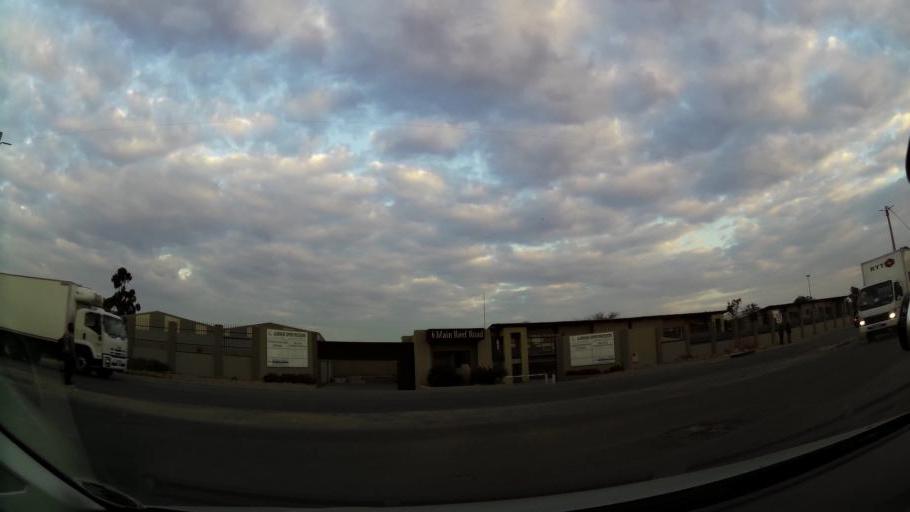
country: ZA
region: Gauteng
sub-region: Ekurhuleni Metropolitan Municipality
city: Germiston
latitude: -26.1983
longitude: 28.1498
